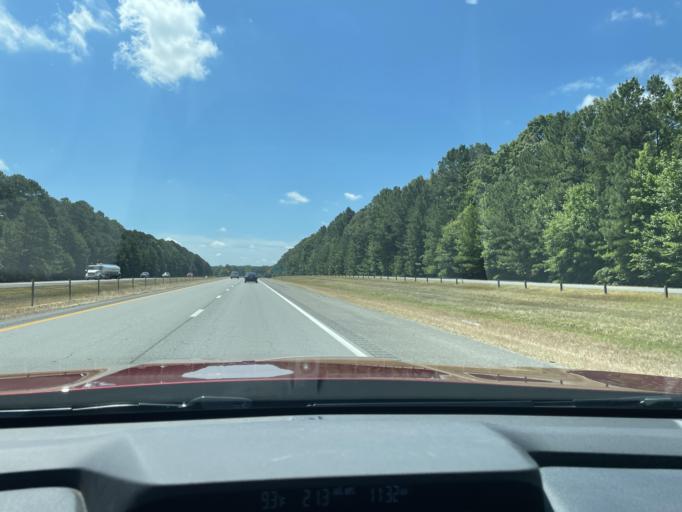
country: US
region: Arkansas
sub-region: Jefferson County
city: Redfield
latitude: 34.5000
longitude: -92.2138
